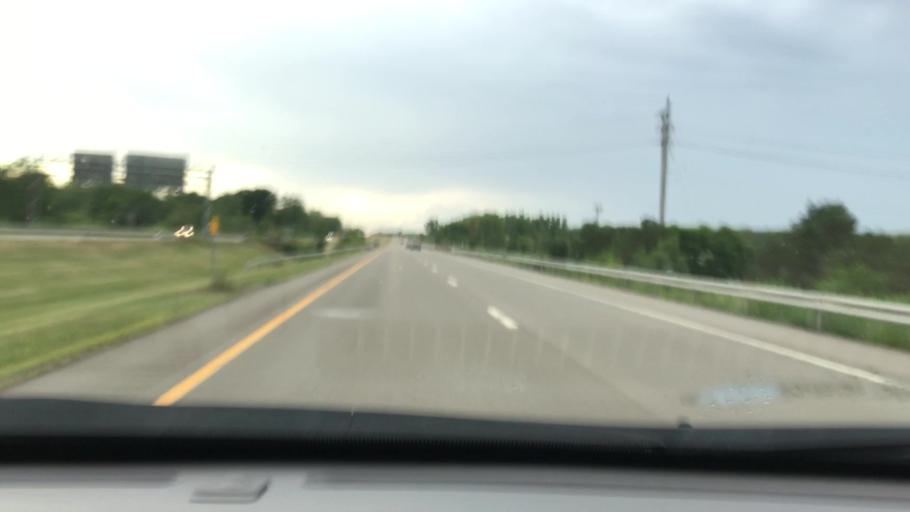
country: US
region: New York
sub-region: Erie County
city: Orchard Park
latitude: 42.7624
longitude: -78.7645
